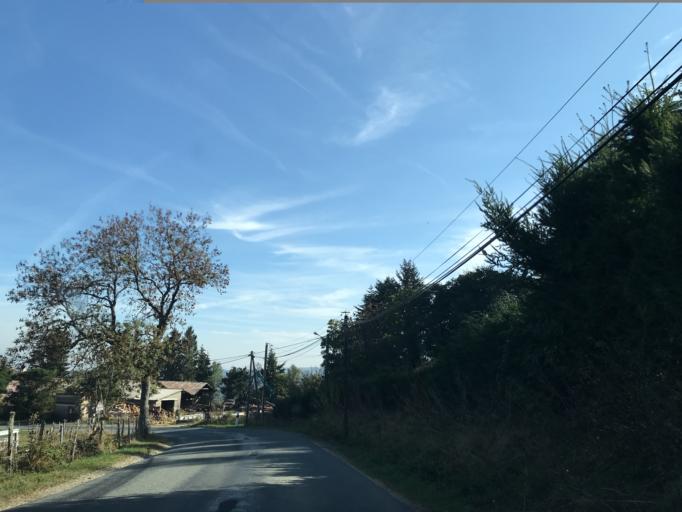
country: FR
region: Rhone-Alpes
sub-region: Departement de la Loire
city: Noiretable
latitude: 45.8092
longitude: 3.7430
